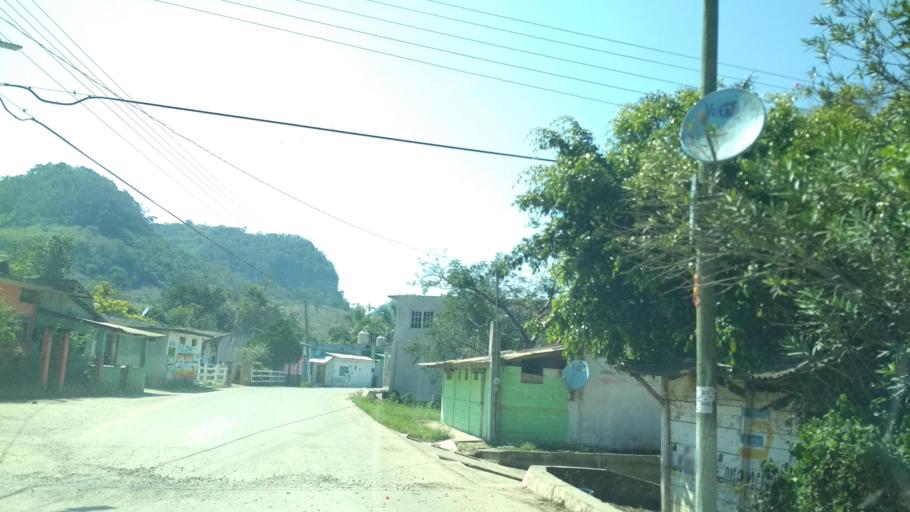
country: MX
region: Veracruz
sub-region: Papantla
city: Polutla
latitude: 20.4761
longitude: -97.2081
